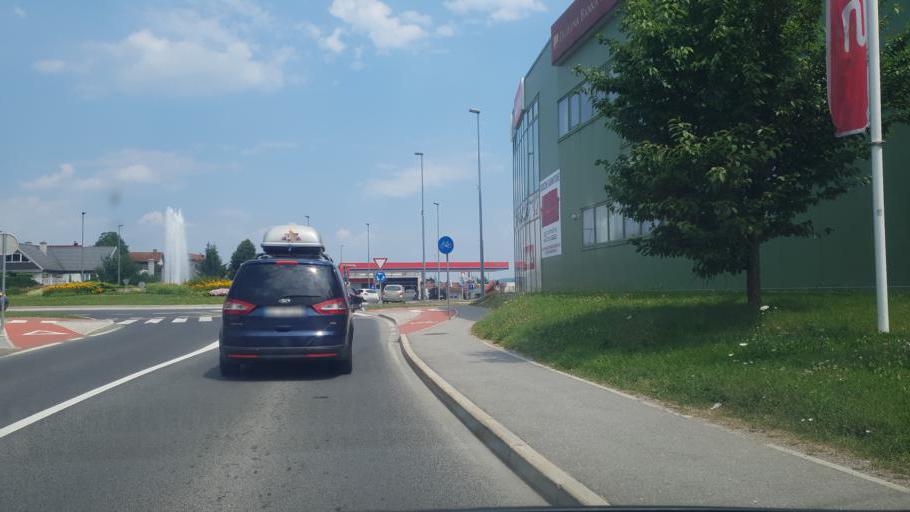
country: SI
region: Pivka
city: Pivka
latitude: 45.6849
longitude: 14.1970
